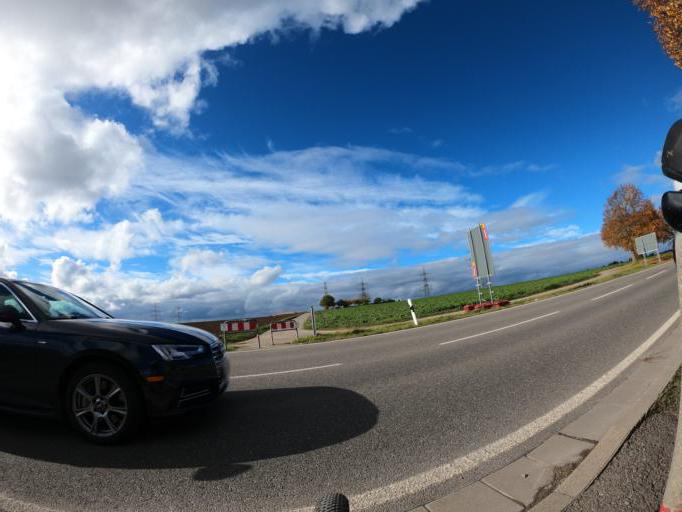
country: DE
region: Baden-Wuerttemberg
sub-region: Regierungsbezirk Stuttgart
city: Magstadt
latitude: 48.7129
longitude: 8.9521
